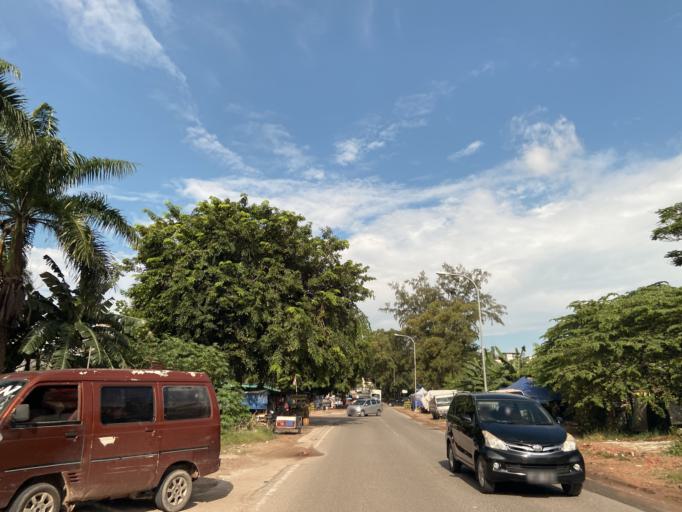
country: SG
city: Singapore
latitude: 1.1118
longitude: 104.0394
